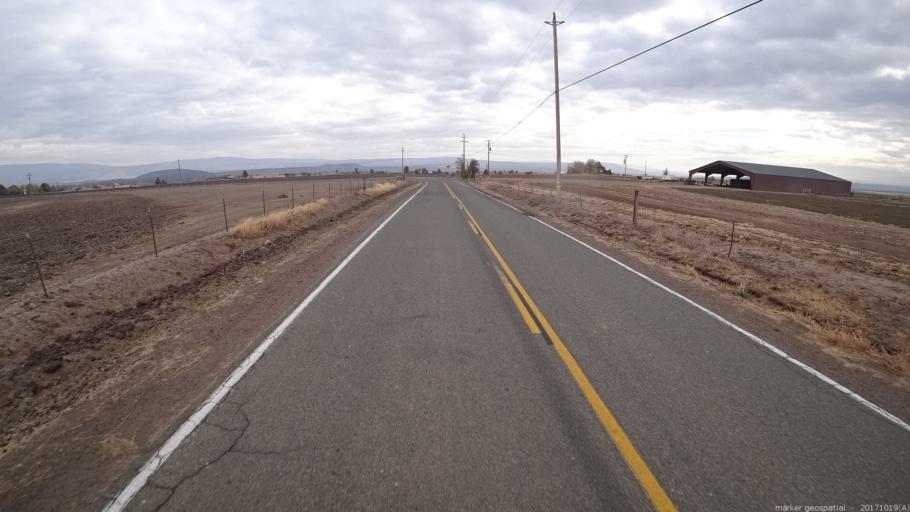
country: US
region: California
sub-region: Shasta County
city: Burney
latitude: 41.0333
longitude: -121.3665
